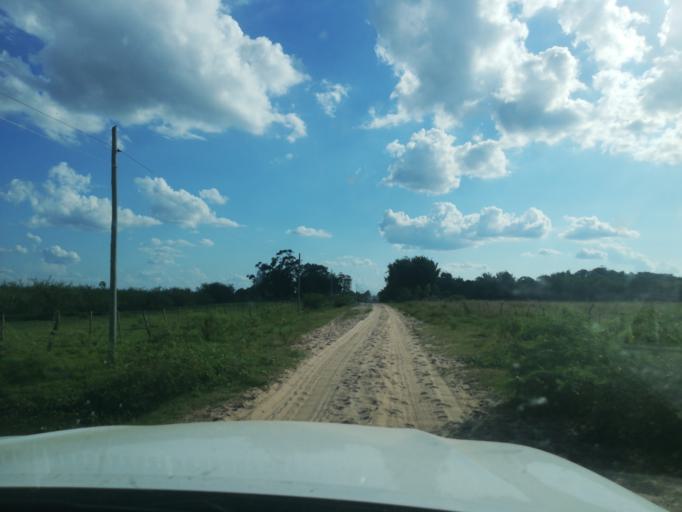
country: AR
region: Corrientes
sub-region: Departamento de San Miguel
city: San Miguel
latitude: -27.9935
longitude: -57.5767
